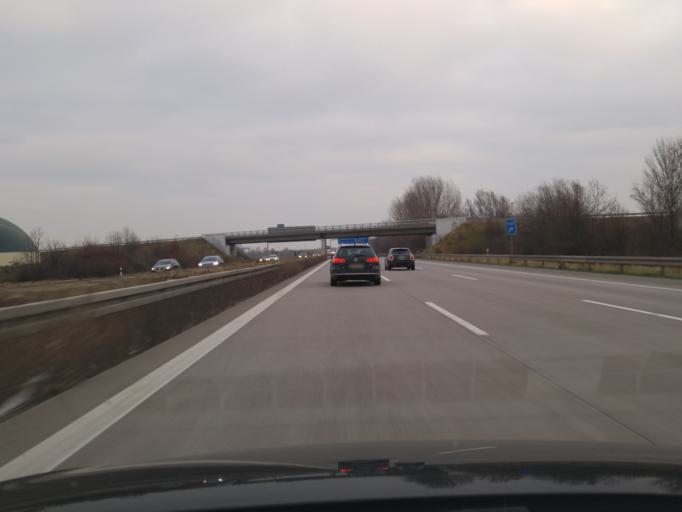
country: DE
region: Saxony-Anhalt
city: Ebendorf
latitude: 52.1731
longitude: 11.5677
